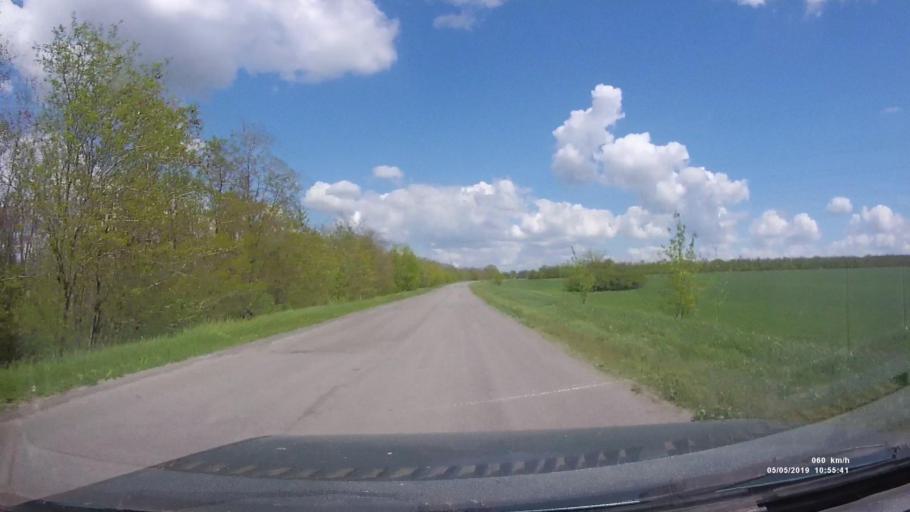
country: RU
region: Rostov
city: Ust'-Donetskiy
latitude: 47.6676
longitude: 40.8206
